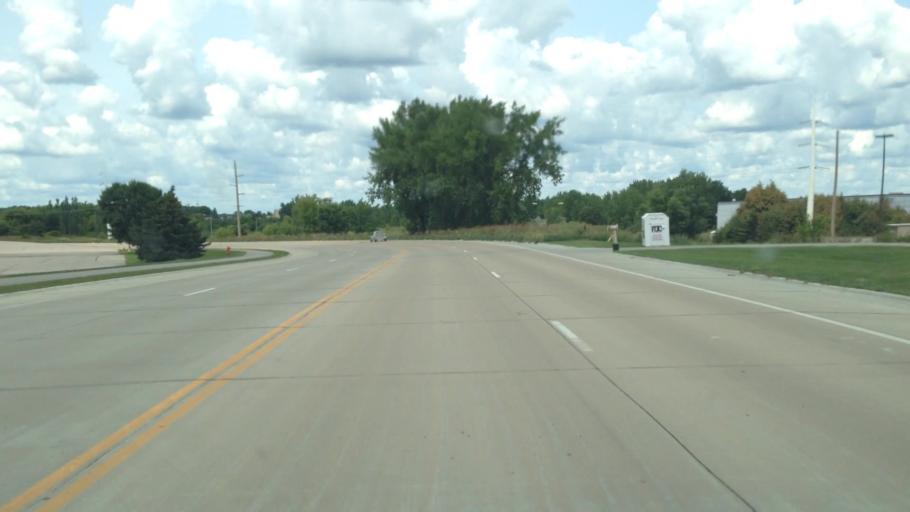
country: US
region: Minnesota
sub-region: Olmsted County
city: Rochester
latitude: 44.0558
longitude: -92.5149
